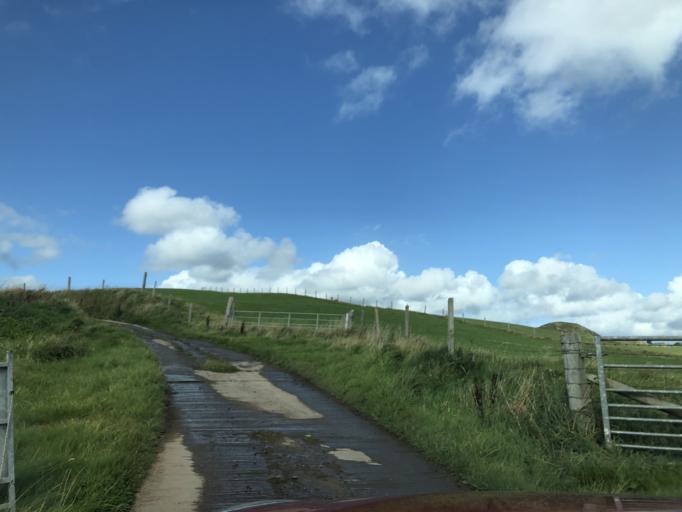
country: GB
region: Scotland
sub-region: Argyll and Bute
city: Campbeltown
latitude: 55.3085
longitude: -5.6071
